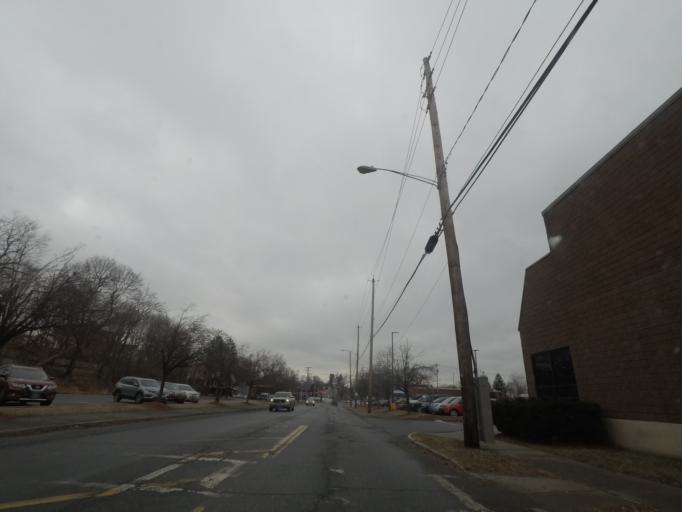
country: US
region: New York
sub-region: Saratoga County
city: Waterford
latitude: 42.7890
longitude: -73.6709
